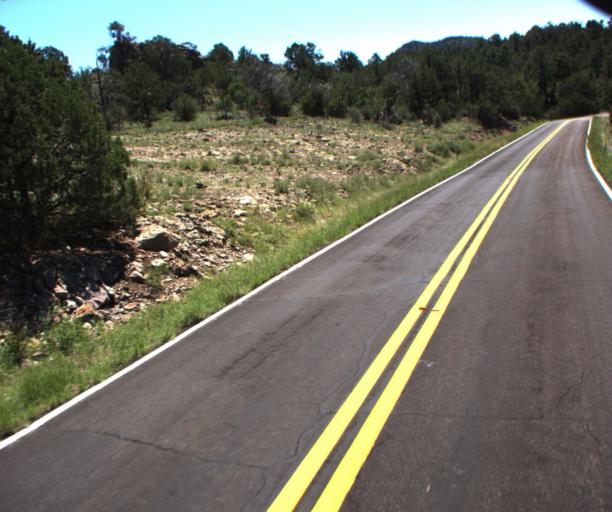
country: US
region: Arizona
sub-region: Greenlee County
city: Morenci
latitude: 33.3864
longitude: -109.3316
